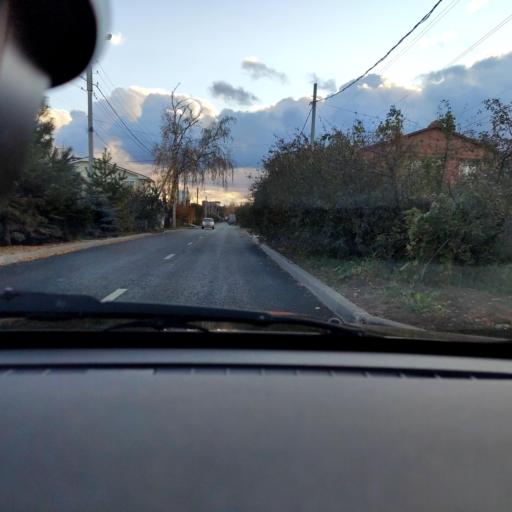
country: RU
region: Samara
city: Tol'yatti
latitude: 53.5287
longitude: 49.4177
